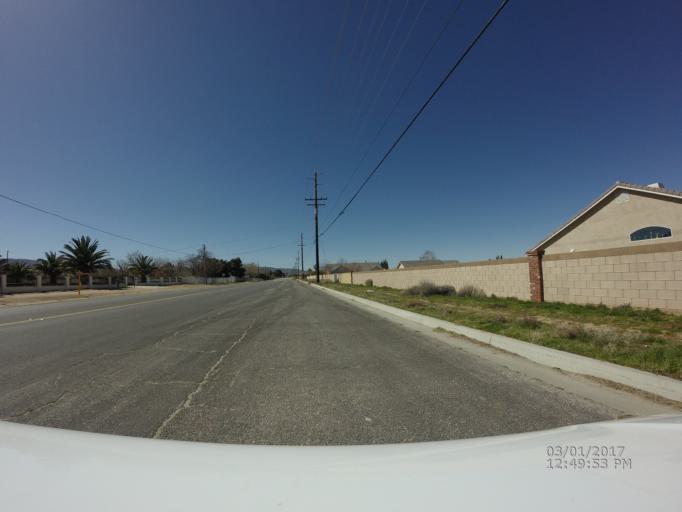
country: US
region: California
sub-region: Los Angeles County
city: Quartz Hill
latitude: 34.6458
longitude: -118.1704
